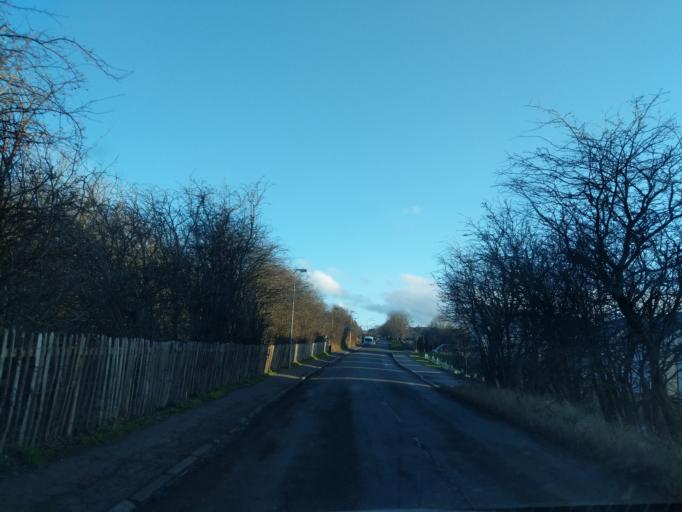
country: GB
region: Scotland
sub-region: Edinburgh
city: Currie
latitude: 55.9009
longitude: -3.3167
